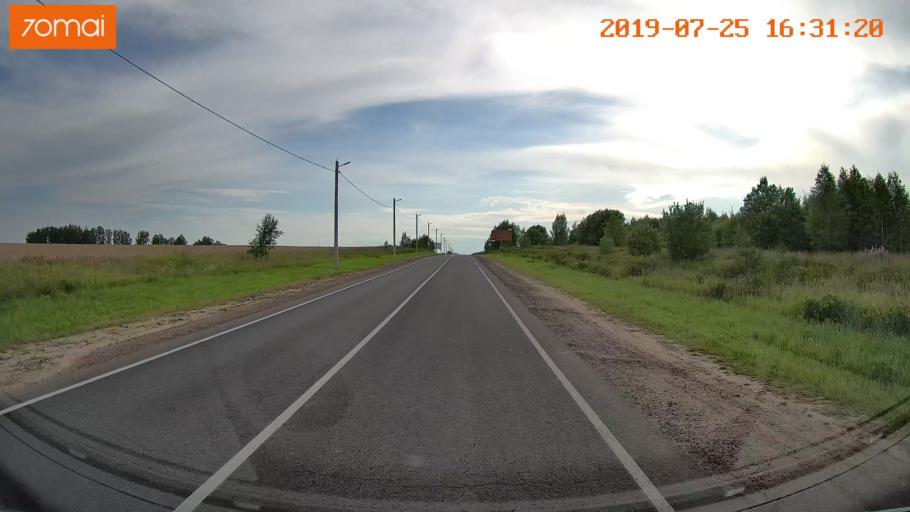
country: RU
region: Ivanovo
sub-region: Privolzhskiy Rayon
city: Ples
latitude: 57.4434
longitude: 41.4867
